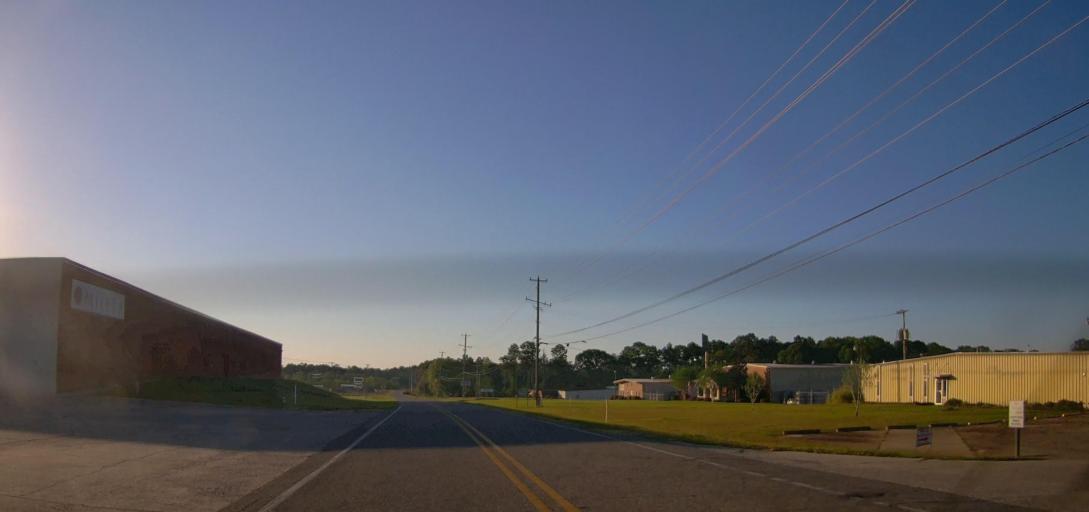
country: US
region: Georgia
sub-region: Ben Hill County
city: Fitzgerald
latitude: 31.6958
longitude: -83.2371
